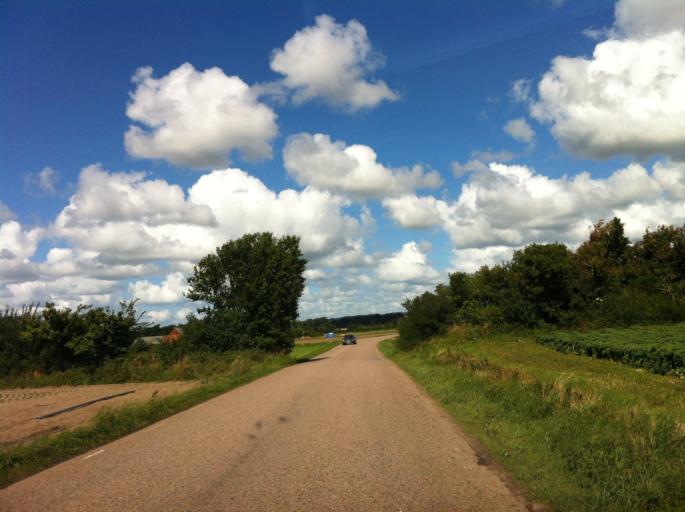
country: SE
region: Skane
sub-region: Angelholms Kommun
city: AEngelholm
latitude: 56.2164
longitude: 12.8574
